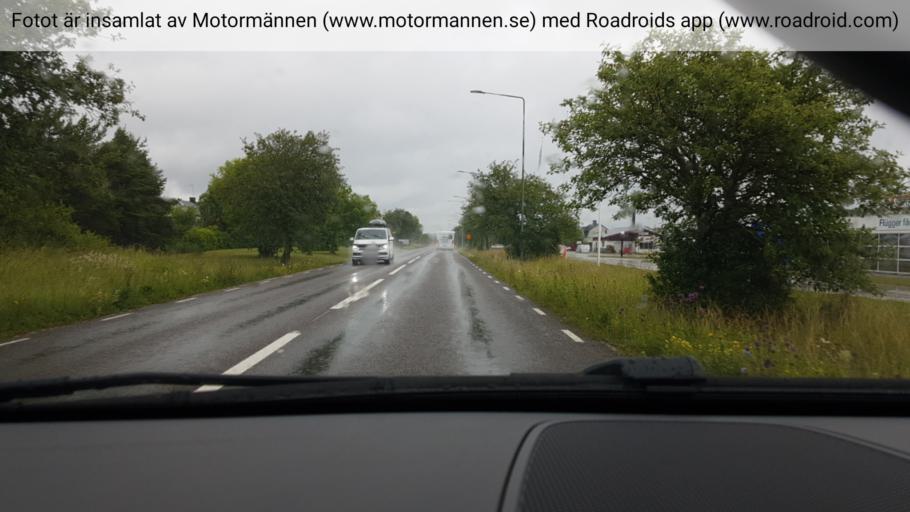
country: SE
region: Gotland
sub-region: Gotland
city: Slite
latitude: 57.6896
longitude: 18.7959
